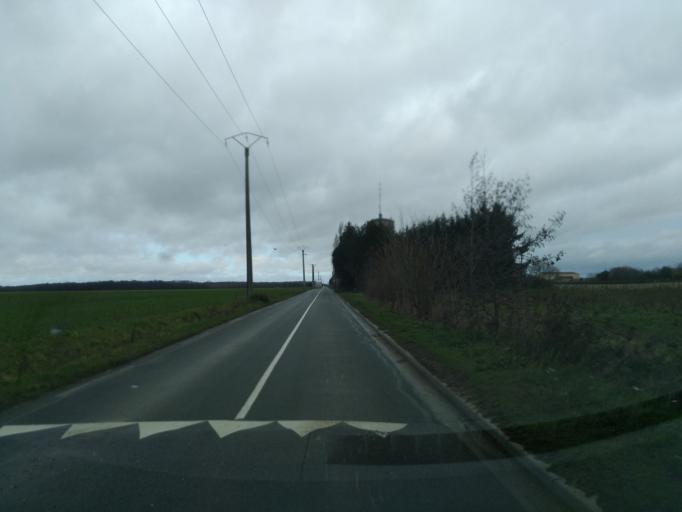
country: FR
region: Ile-de-France
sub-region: Departement des Yvelines
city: Feucherolles
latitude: 48.8912
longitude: 1.9668
